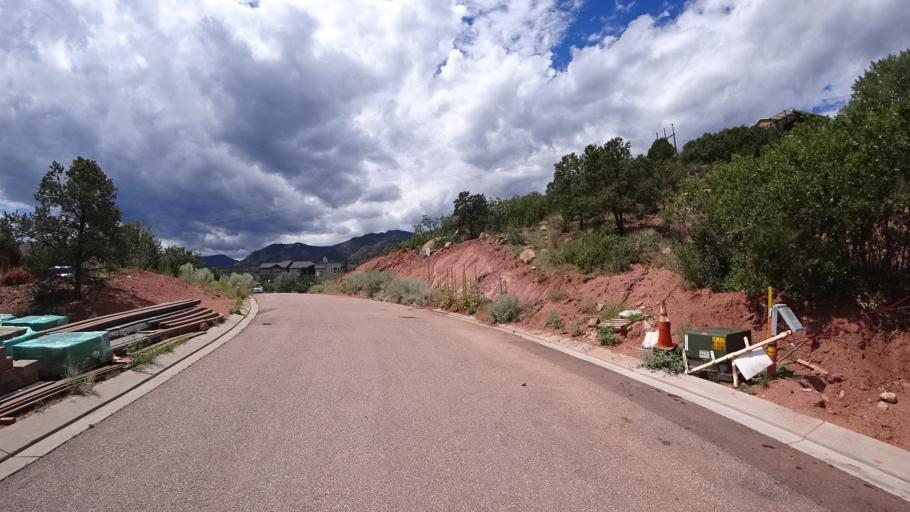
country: US
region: Colorado
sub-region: El Paso County
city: Manitou Springs
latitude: 38.8538
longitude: -104.8875
